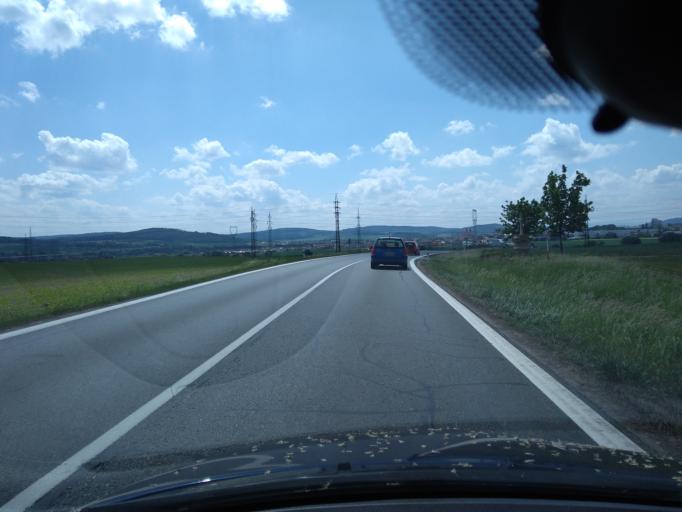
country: CZ
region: Plzensky
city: Prestice
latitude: 49.5936
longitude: 13.3275
